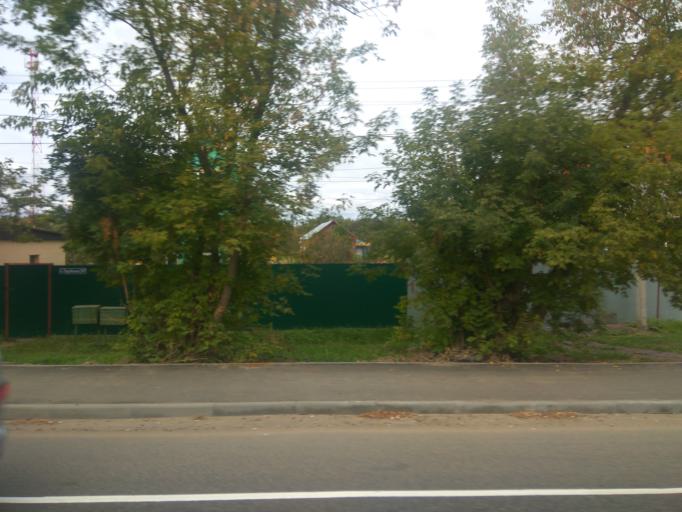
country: RU
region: Moskovskaya
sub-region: Shchelkovskiy Rayon
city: Grebnevo
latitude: 55.9847
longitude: 38.1230
